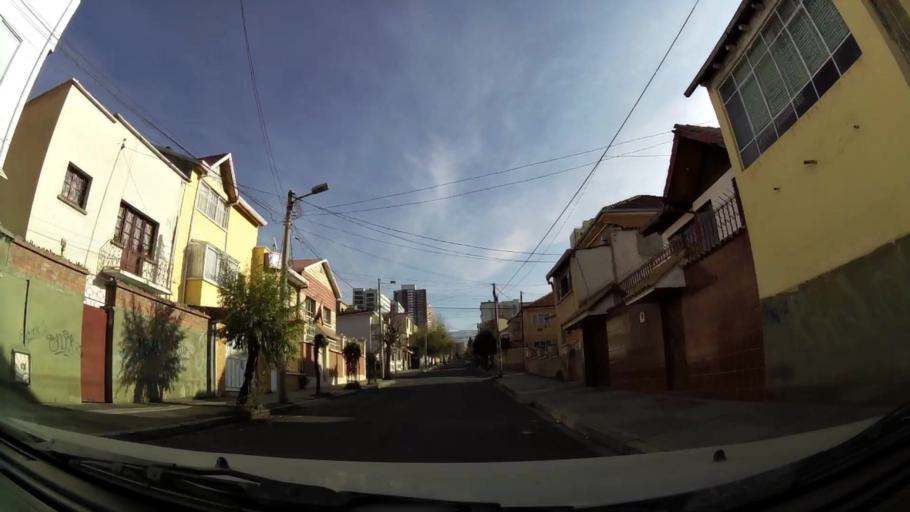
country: BO
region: La Paz
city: La Paz
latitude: -16.5056
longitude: -68.1180
